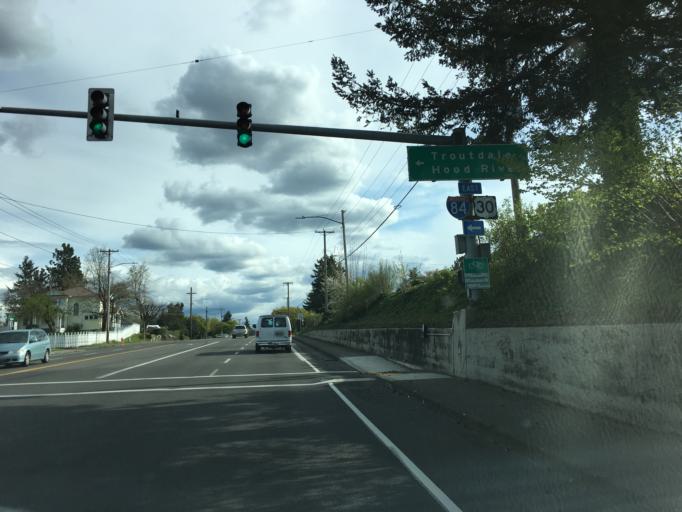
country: US
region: Oregon
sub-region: Multnomah County
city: Lents
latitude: 45.5452
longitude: -122.5375
